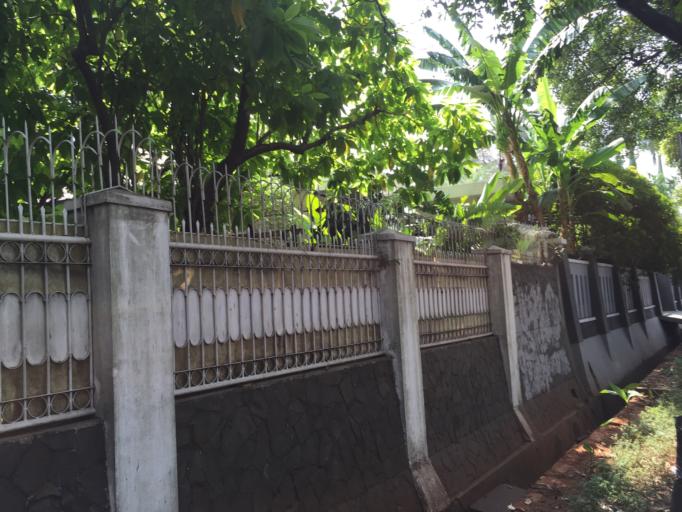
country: ID
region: Jakarta Raya
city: Jakarta
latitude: -6.2044
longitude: 106.8334
